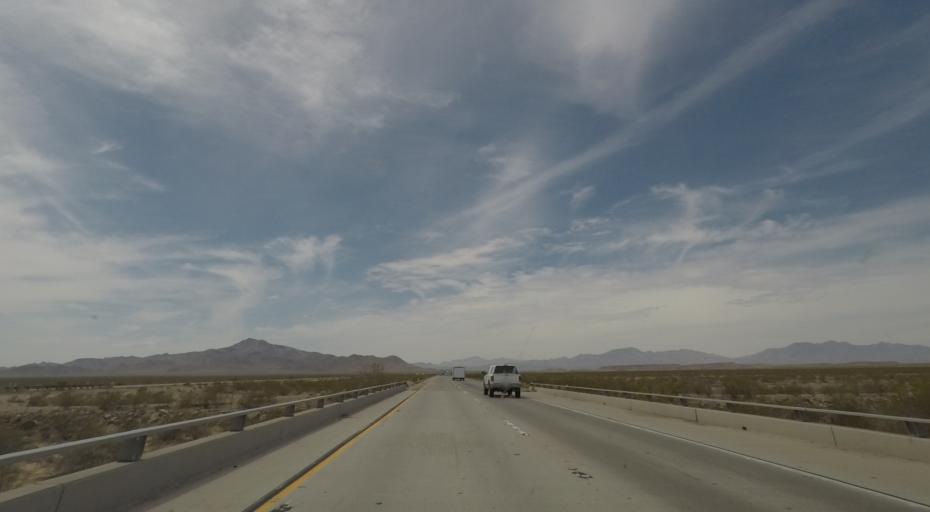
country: US
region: California
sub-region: San Bernardino County
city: Needles
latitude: 34.8065
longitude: -115.2561
